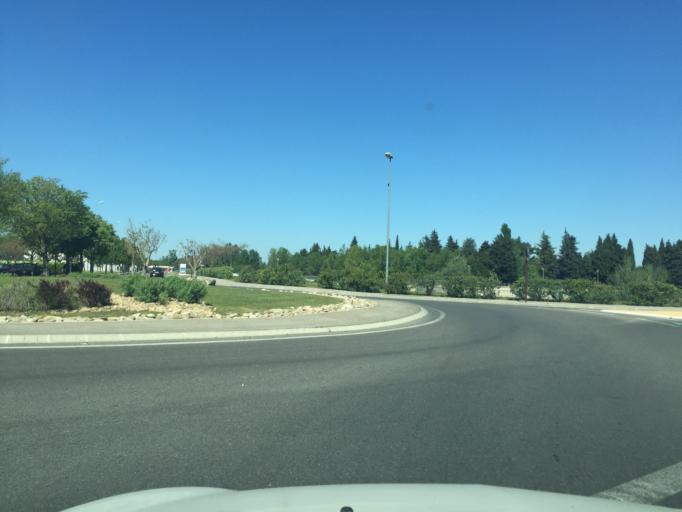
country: FR
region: Provence-Alpes-Cote d'Azur
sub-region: Departement du Vaucluse
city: Montfavet
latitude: 43.9245
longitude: 4.8622
